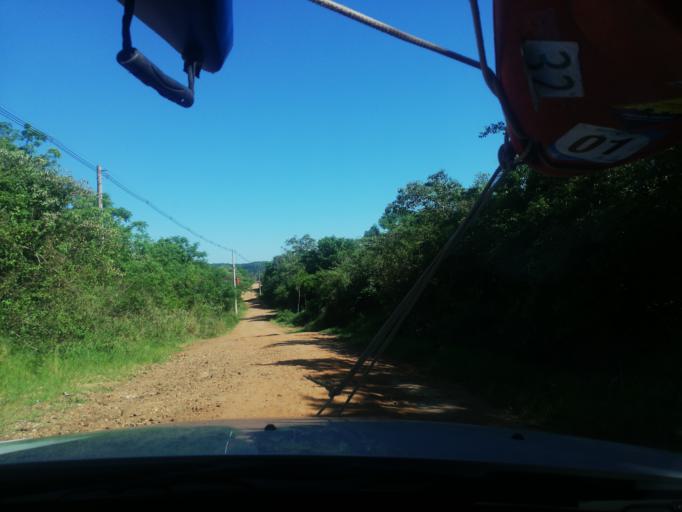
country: AR
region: Misiones
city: Santa Ana
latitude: -27.3352
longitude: -55.5819
